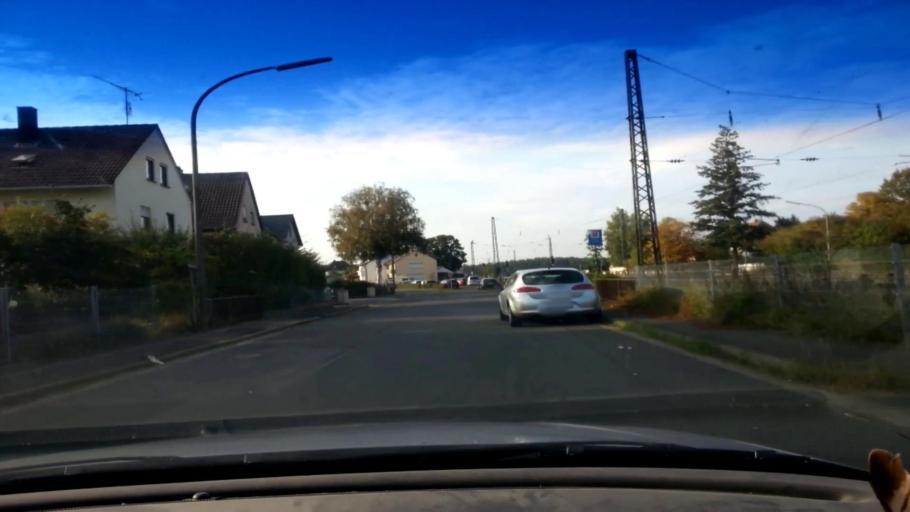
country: DE
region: Bavaria
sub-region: Upper Franconia
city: Hirschaid
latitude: 49.8202
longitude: 10.9901
